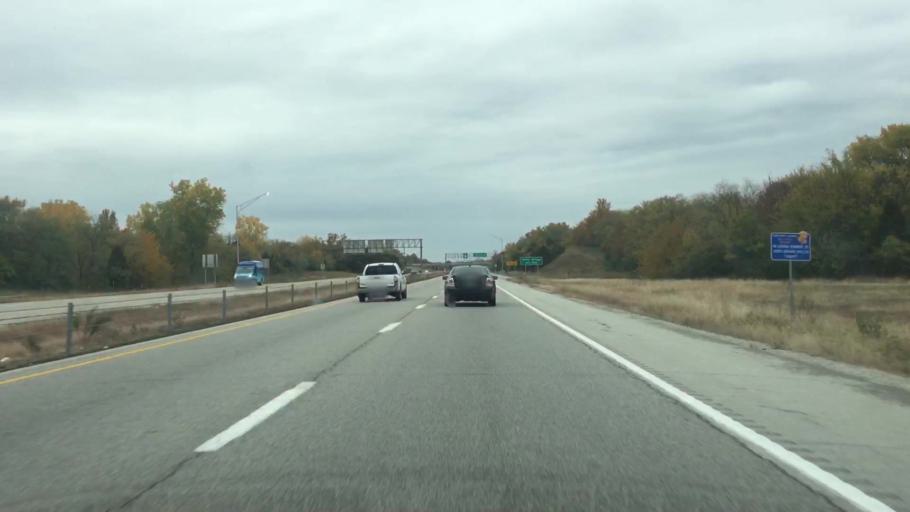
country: US
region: Missouri
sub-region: Jackson County
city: Lees Summit
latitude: 38.9364
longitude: -94.4068
